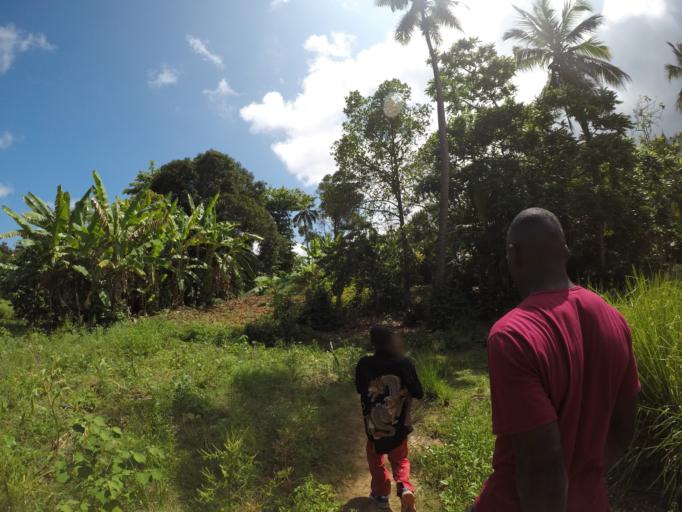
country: TZ
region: Pemba South
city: Mtambile
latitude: -5.3992
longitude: 39.7388
